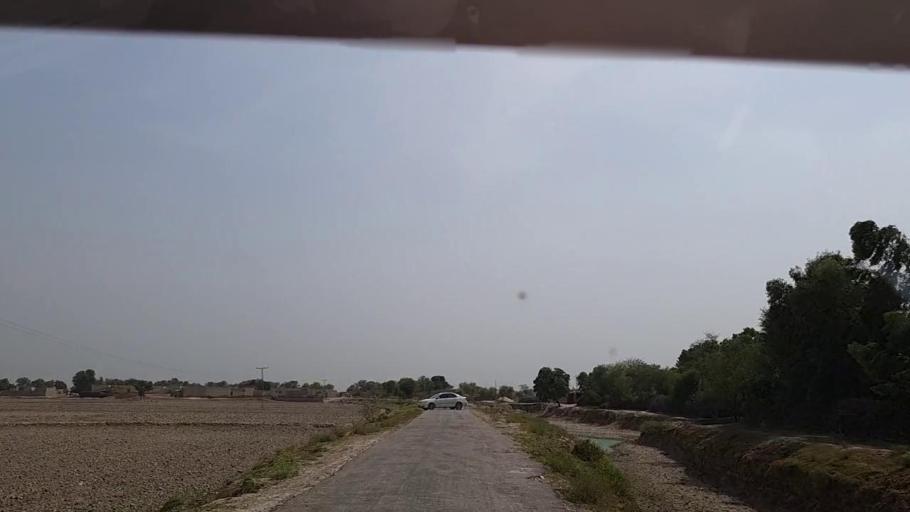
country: PK
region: Sindh
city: Khairpur Nathan Shah
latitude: 27.0684
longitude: 67.6879
